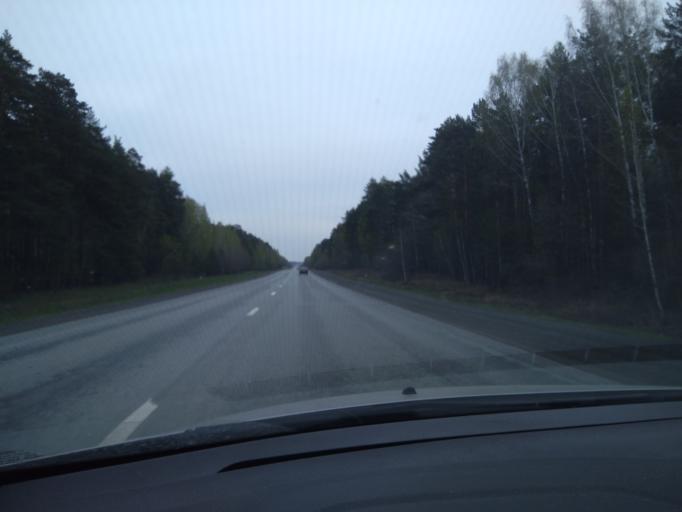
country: RU
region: Sverdlovsk
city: Baraba
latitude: 56.7805
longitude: 61.7870
